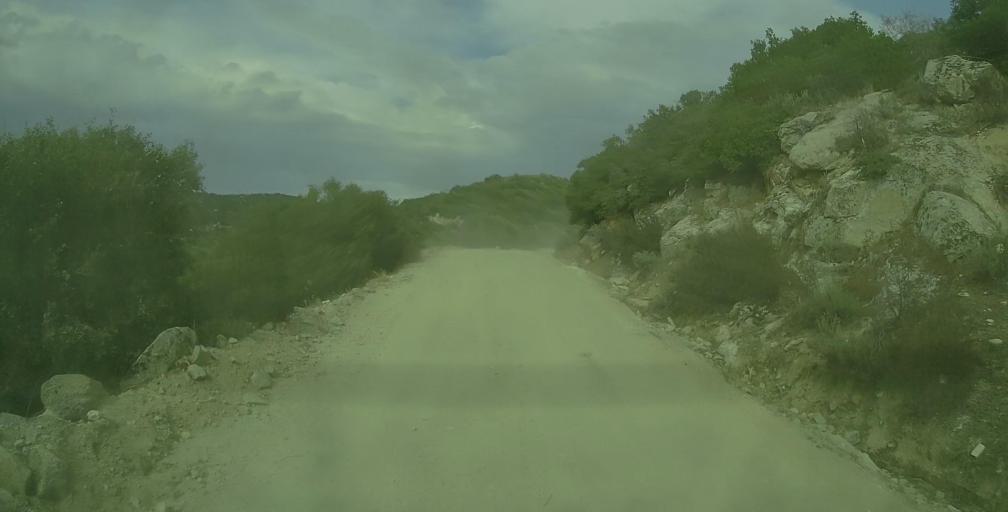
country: GR
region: Central Macedonia
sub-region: Nomos Chalkidikis
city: Sykia
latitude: 39.9924
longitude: 23.9159
